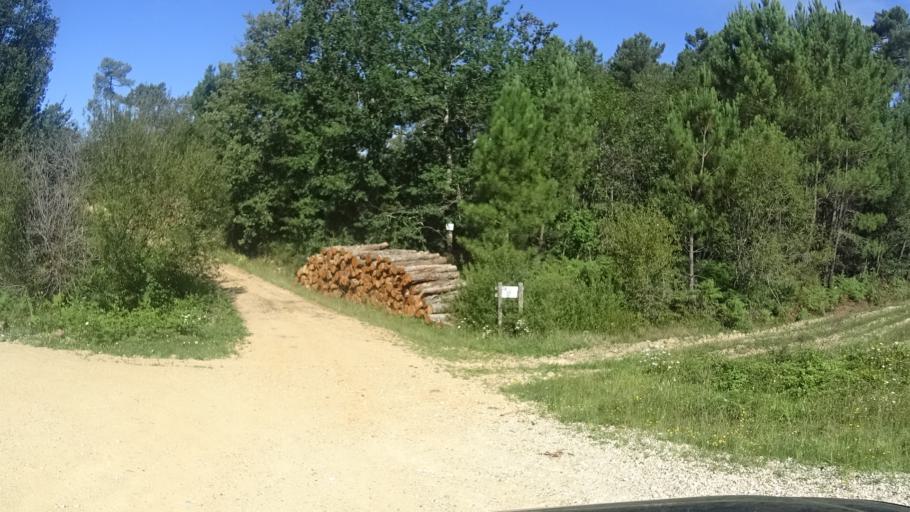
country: FR
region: Aquitaine
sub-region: Departement de la Dordogne
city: Sourzac
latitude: 45.0333
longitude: 0.3998
